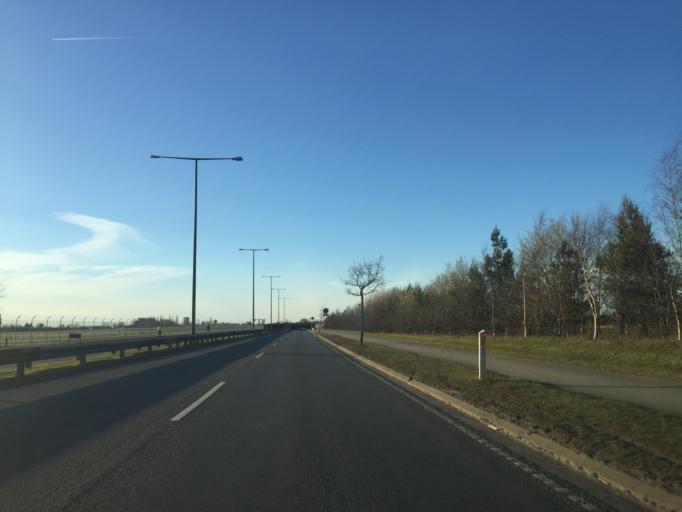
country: DK
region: Capital Region
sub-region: Tarnby Kommune
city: Tarnby
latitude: 55.5993
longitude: 12.6241
